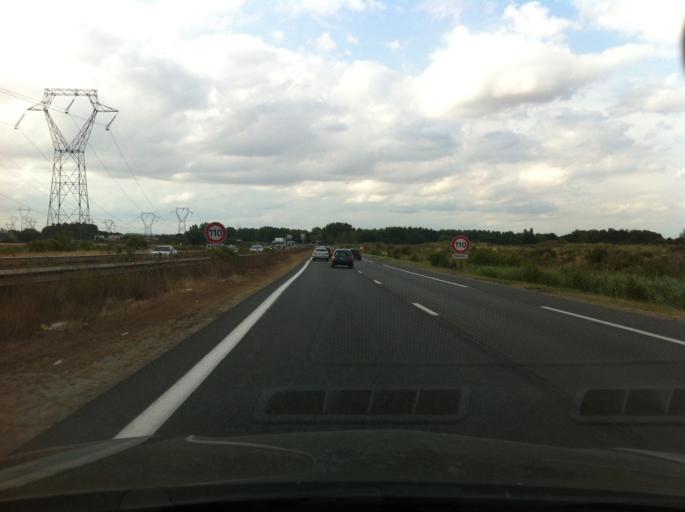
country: FR
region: Ile-de-France
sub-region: Departement de Seine-et-Marne
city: Villeparisis
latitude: 48.9457
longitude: 2.6287
